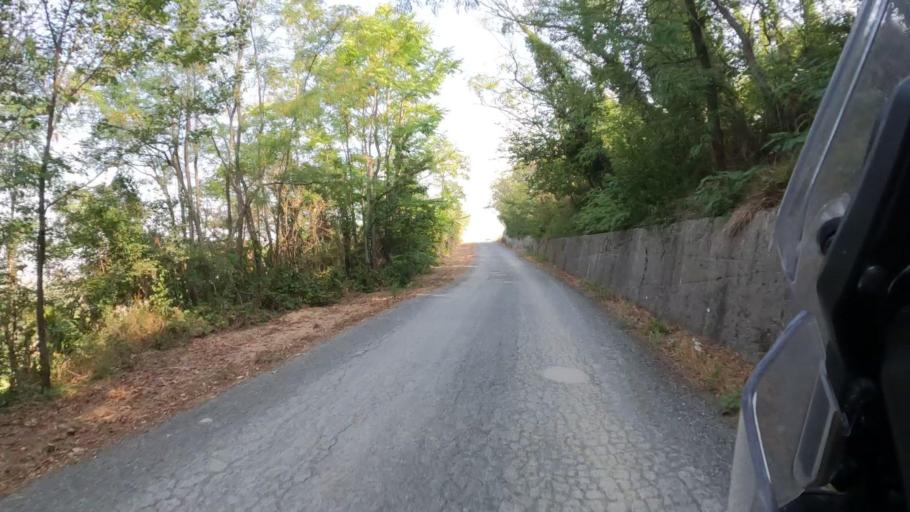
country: IT
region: Piedmont
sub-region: Provincia di Asti
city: Castel Boglione
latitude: 44.7480
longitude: 8.3874
